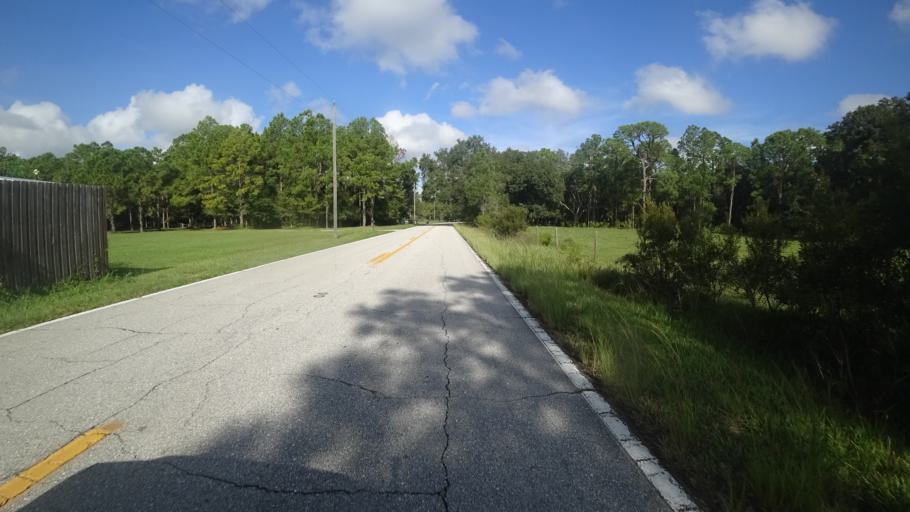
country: US
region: Florida
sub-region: Hardee County
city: Wauchula
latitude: 27.4698
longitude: -82.0771
